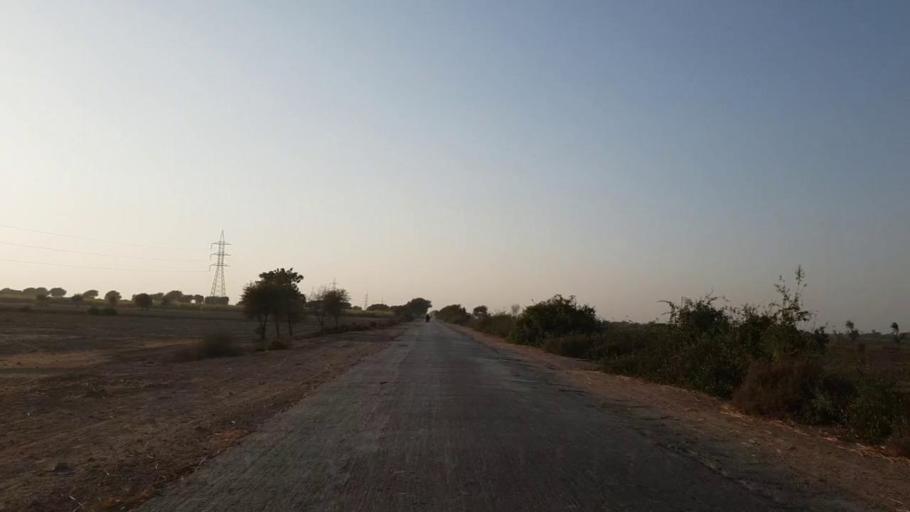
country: PK
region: Sindh
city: Chambar
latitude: 25.2176
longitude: 68.7548
